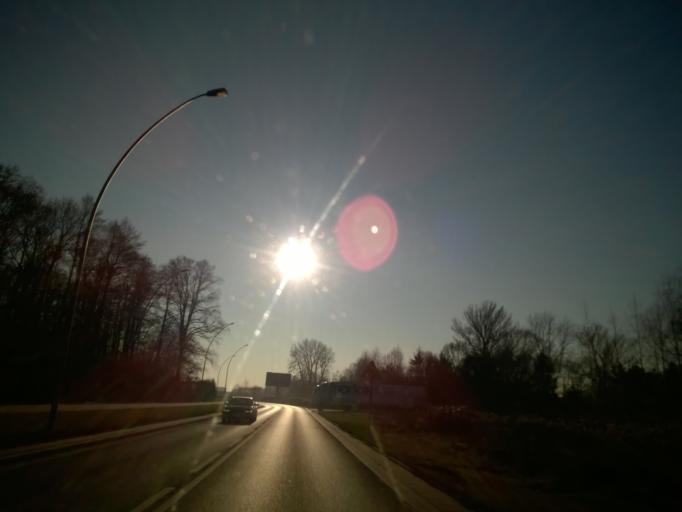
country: PL
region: Lower Silesian Voivodeship
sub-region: Powiat wroclawski
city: Bielany Wroclawskie
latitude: 51.0622
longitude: 16.9564
